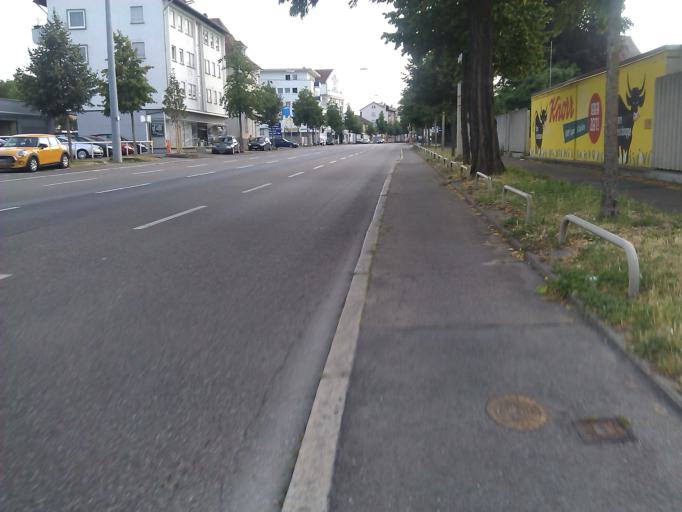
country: DE
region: Baden-Wuerttemberg
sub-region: Regierungsbezirk Stuttgart
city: Heilbronn
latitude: 49.1308
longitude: 9.2155
